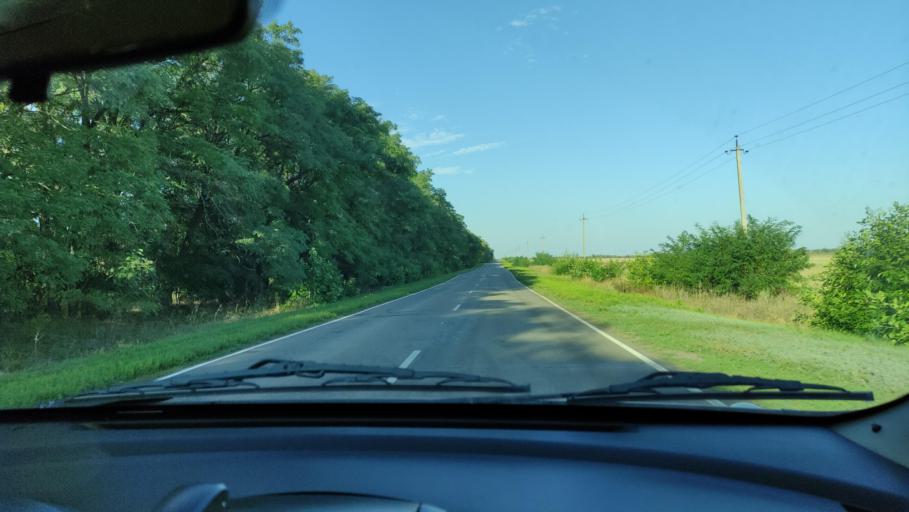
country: RU
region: Voronezj
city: Verkhniy Mamon
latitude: 50.1310
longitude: 40.3249
